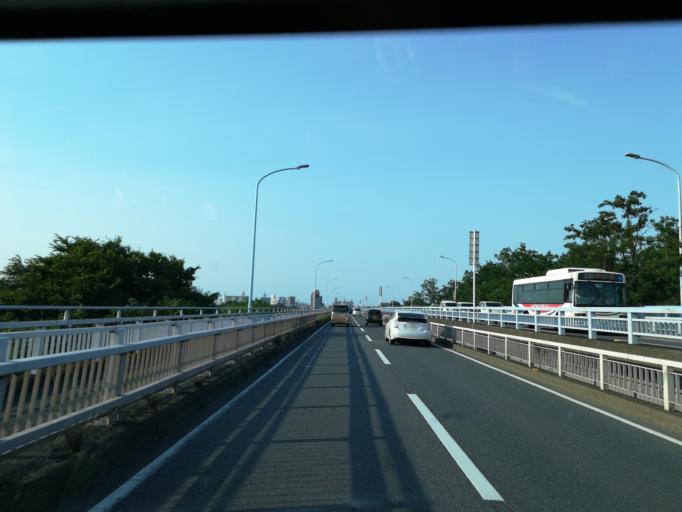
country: JP
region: Saitama
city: Kumagaya
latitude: 36.1311
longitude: 139.3768
